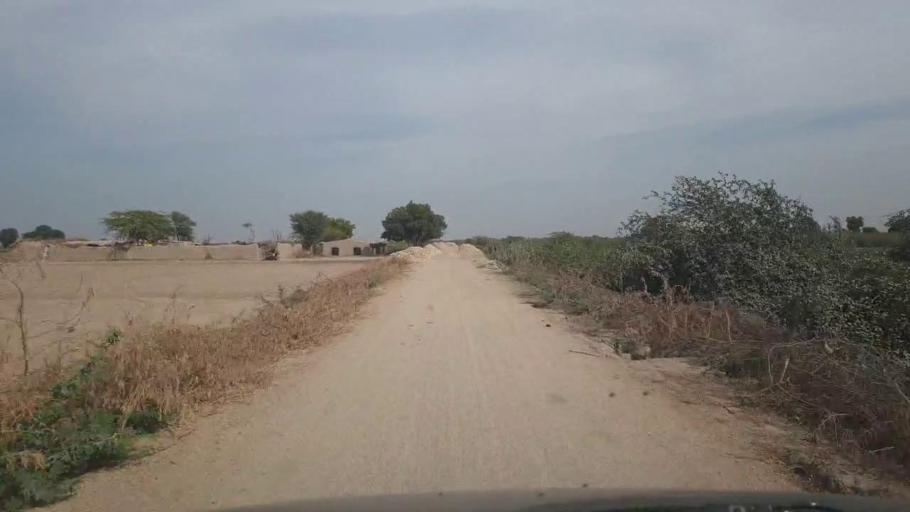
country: PK
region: Sindh
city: Kunri
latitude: 25.2295
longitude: 69.5956
